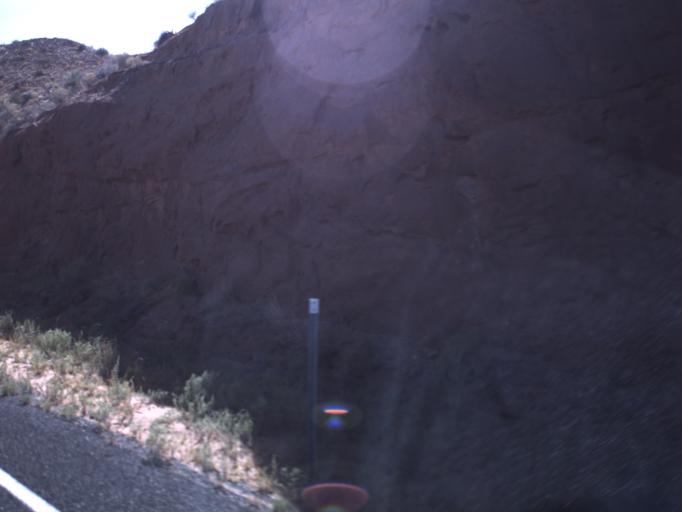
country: US
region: Utah
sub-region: Wayne County
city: Loa
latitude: 38.1359
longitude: -110.6098
